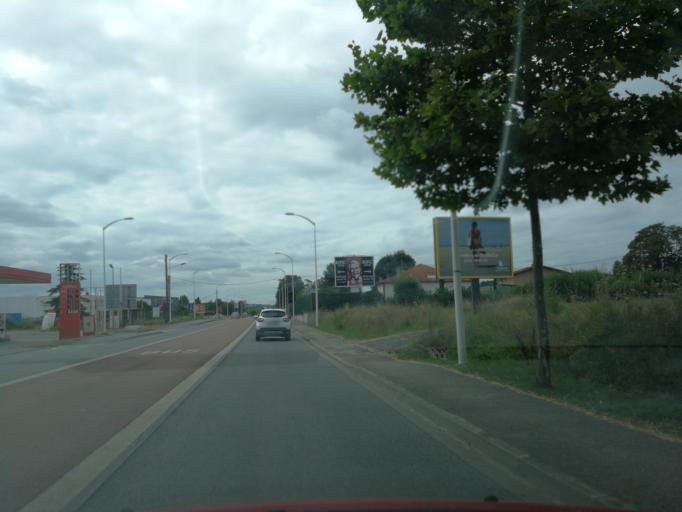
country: FR
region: Midi-Pyrenees
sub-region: Departement de la Haute-Garonne
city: Balma
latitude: 43.5894
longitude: 1.5147
